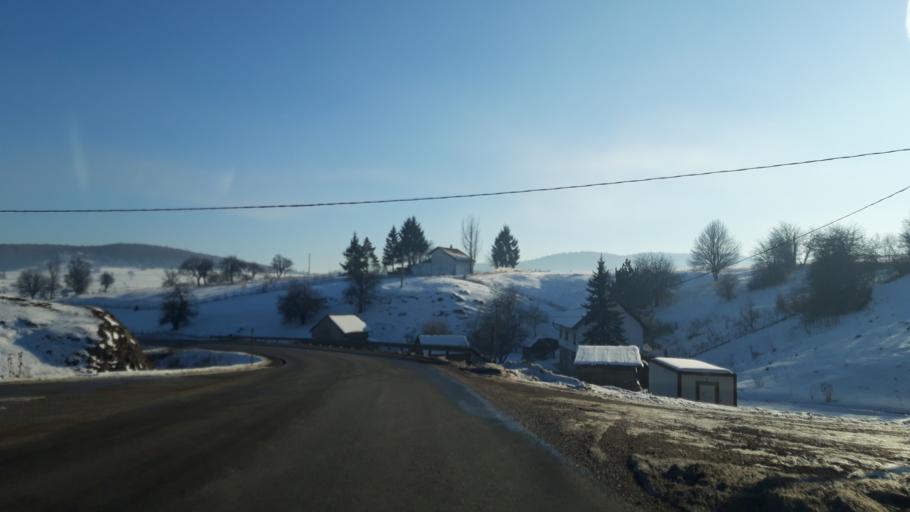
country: BA
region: Republika Srpska
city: Sokolac
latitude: 43.9208
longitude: 18.7572
